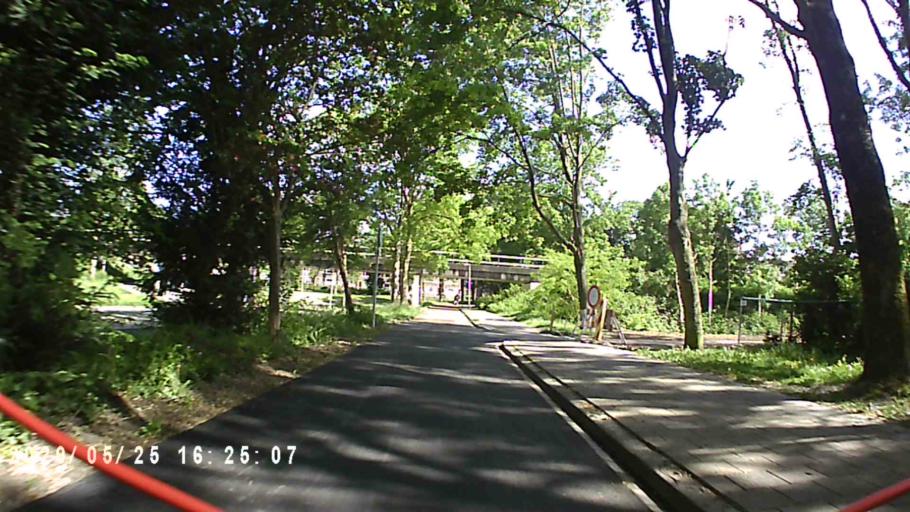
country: NL
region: Groningen
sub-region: Gemeente Groningen
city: Groningen
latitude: 53.2243
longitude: 6.5469
